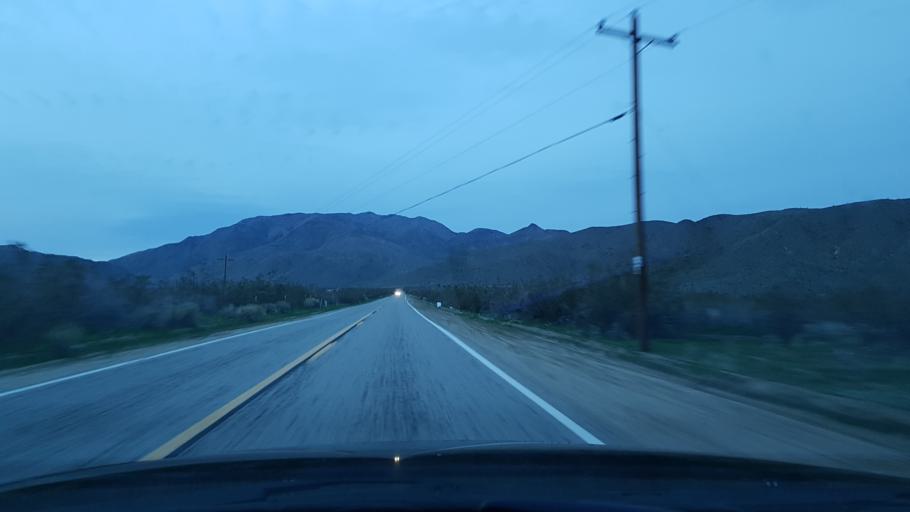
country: US
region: California
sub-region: San Diego County
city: Pine Valley
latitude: 32.9828
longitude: -116.4411
